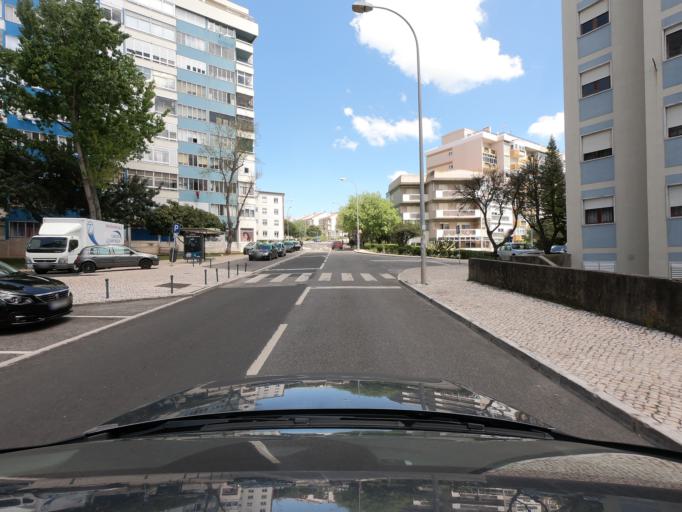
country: PT
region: Lisbon
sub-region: Oeiras
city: Oeiras
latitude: 38.6950
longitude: -9.3071
